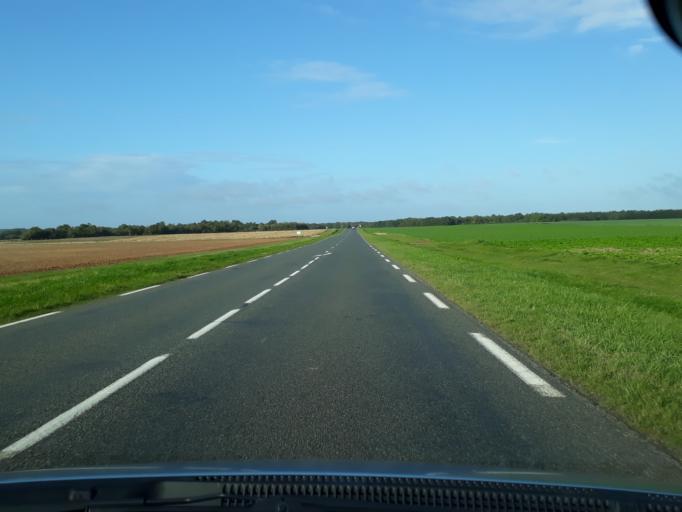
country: FR
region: Centre
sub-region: Departement du Loiret
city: Malesherbes
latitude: 48.3066
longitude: 2.4609
